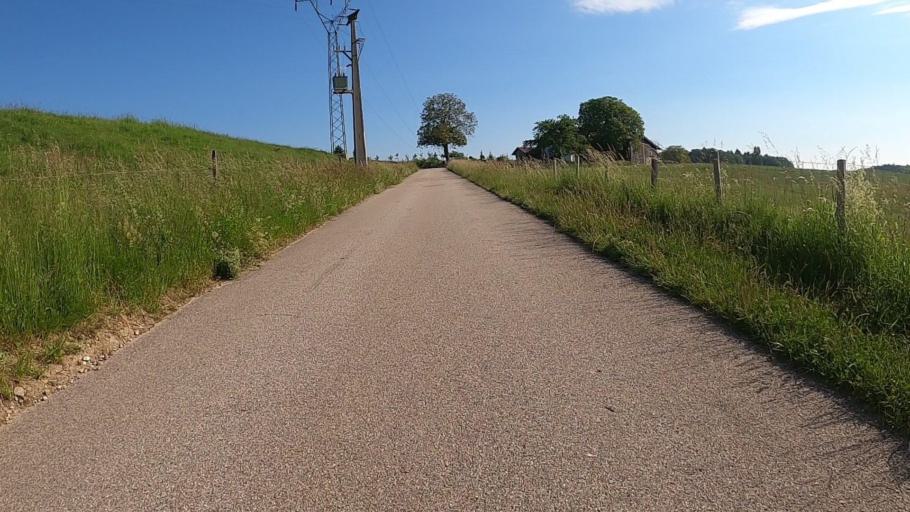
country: CH
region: Vaud
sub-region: Nyon District
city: Rolle
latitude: 46.4821
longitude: 6.3359
